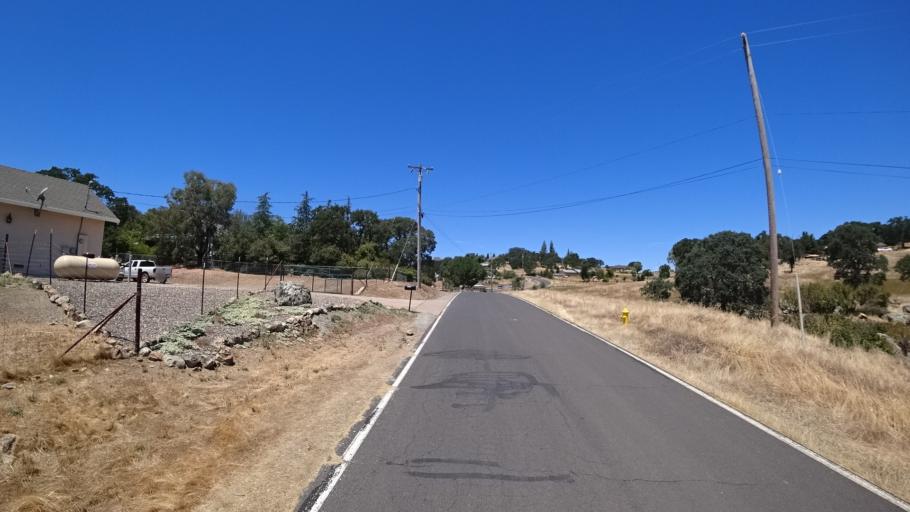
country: US
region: California
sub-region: Calaveras County
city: Rancho Calaveras
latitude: 38.1477
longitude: -120.8436
